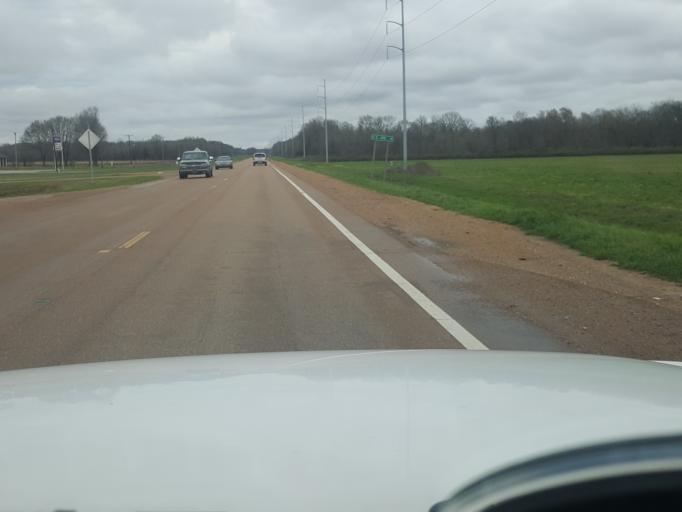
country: US
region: Mississippi
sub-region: Yazoo County
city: Yazoo City
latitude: 32.8621
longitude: -90.4269
